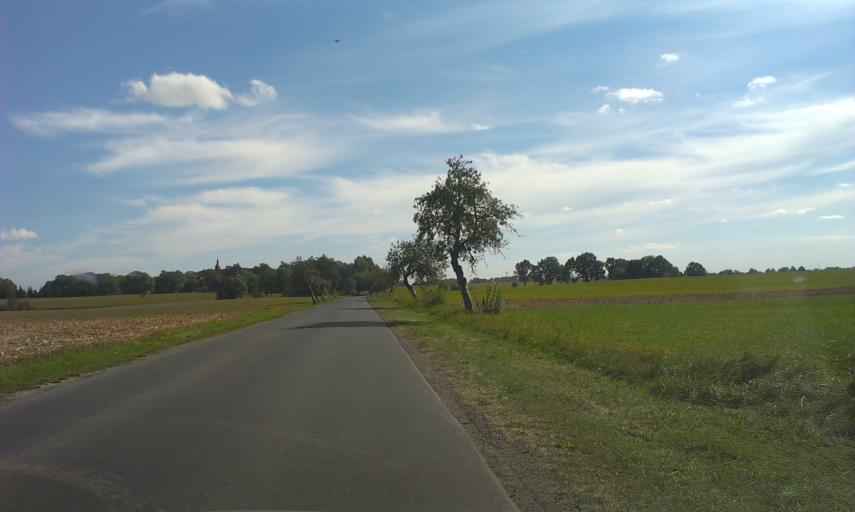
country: PL
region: Greater Poland Voivodeship
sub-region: Powiat pilski
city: Lobzenica
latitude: 53.2733
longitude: 17.2301
